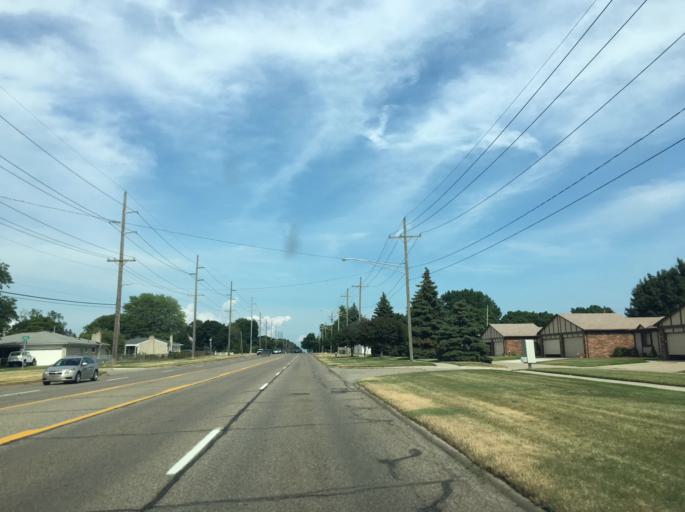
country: US
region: Michigan
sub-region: Macomb County
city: Fraser
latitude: 42.5381
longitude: -82.9784
